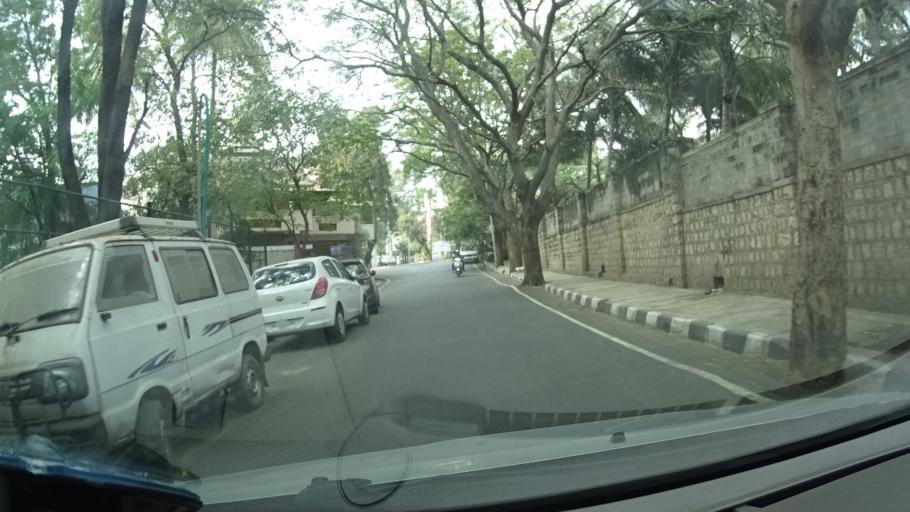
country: IN
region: Karnataka
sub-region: Bangalore Urban
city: Bangalore
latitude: 13.0056
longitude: 77.5521
